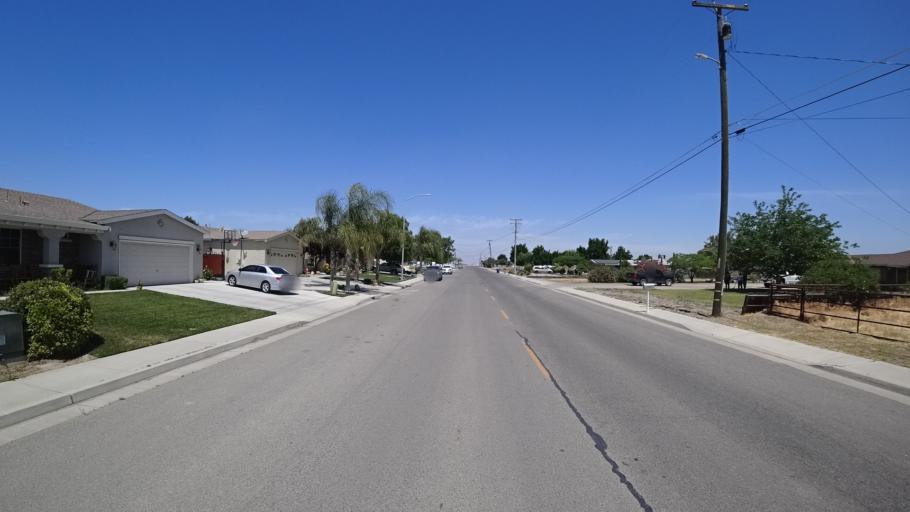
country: US
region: California
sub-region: Kings County
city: Corcoran
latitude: 36.1136
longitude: -119.5722
